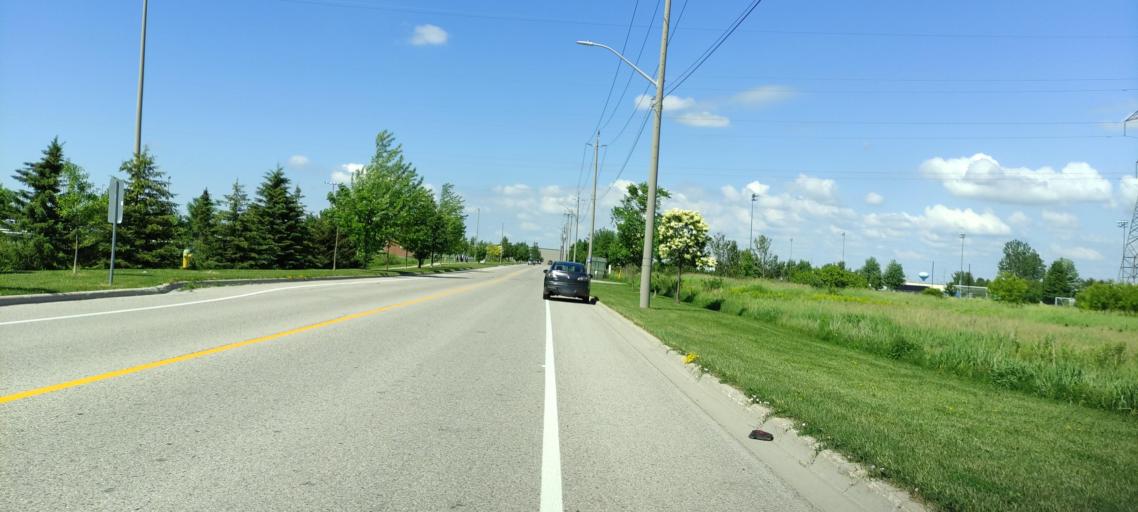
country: CA
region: Ontario
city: Stratford
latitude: 43.3464
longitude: -81.0098
